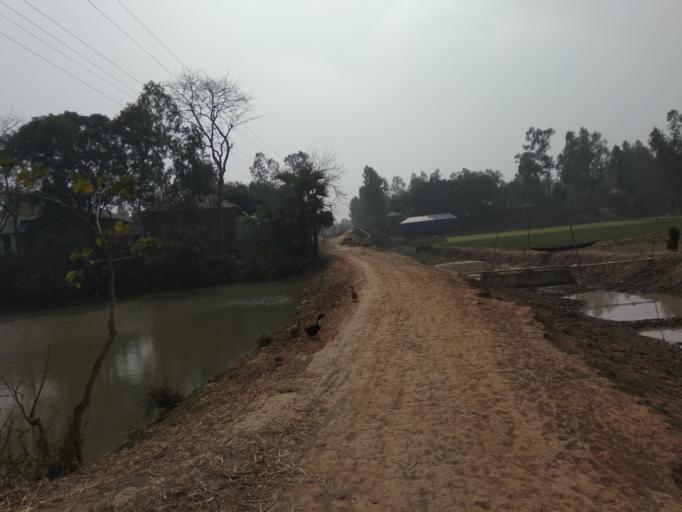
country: BD
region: Rajshahi
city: Ishurdi
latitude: 24.4666
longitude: 89.2670
